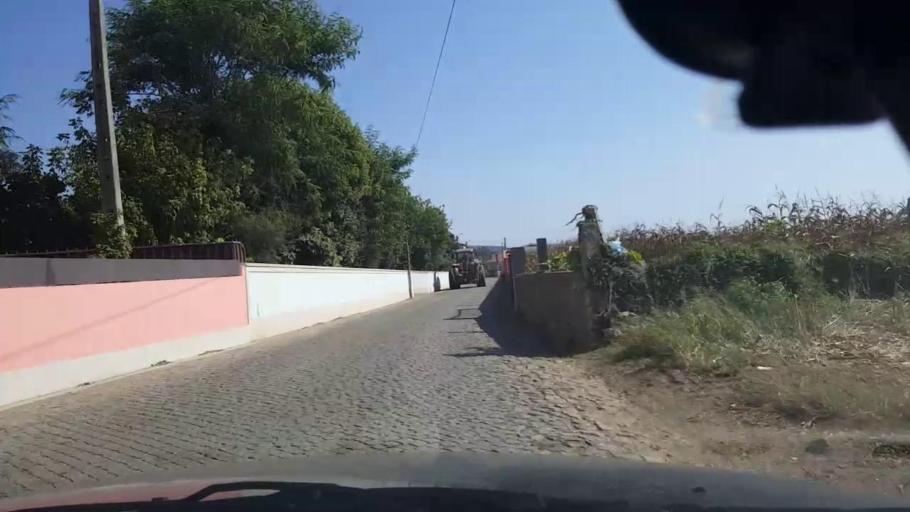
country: PT
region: Porto
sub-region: Povoa de Varzim
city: Pedroso
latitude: 41.4117
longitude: -8.6966
